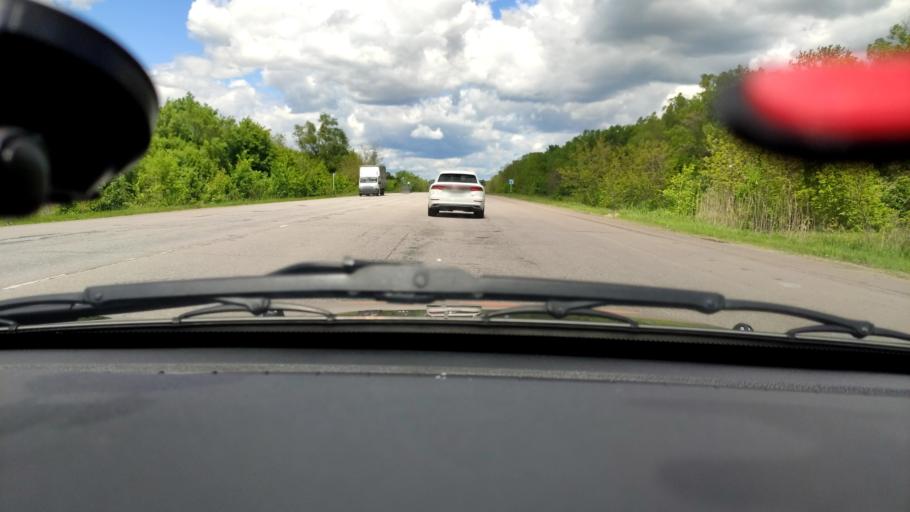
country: RU
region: Voronezj
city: Uryv-Pokrovka
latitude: 51.2325
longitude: 39.0593
